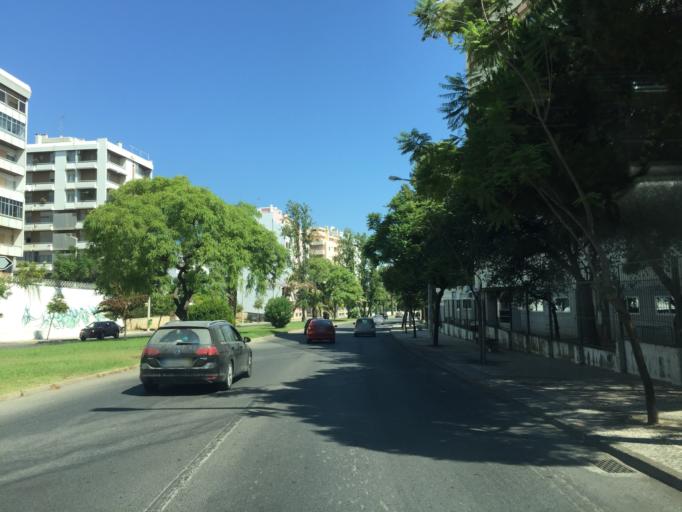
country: PT
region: Faro
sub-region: Faro
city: Faro
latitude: 37.0257
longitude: -7.9297
